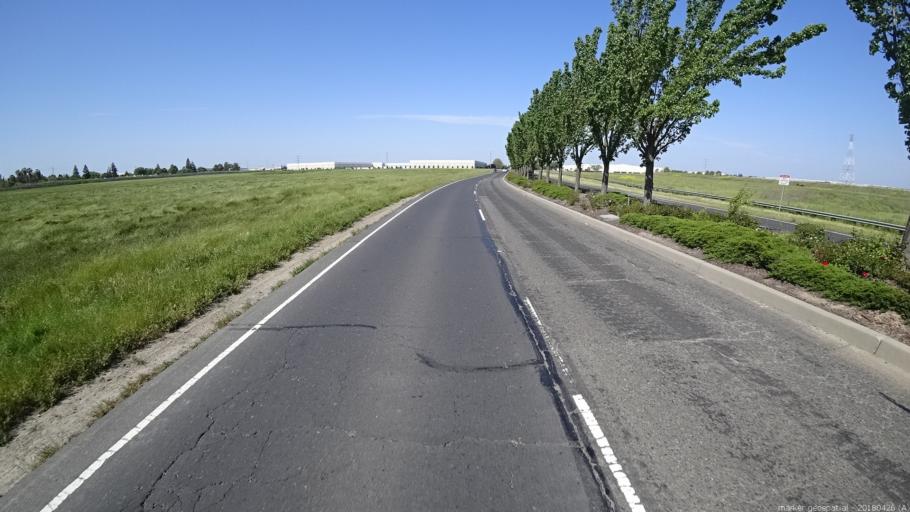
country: US
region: California
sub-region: Yolo County
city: West Sacramento
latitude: 38.5556
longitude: -121.5538
